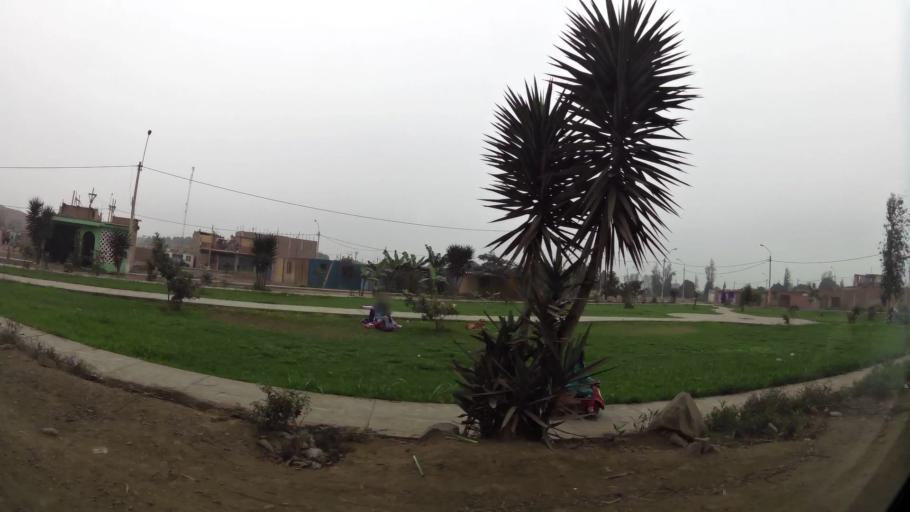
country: PE
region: Lima
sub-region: Lima
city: Carabayllo
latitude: -11.8609
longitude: -77.0180
